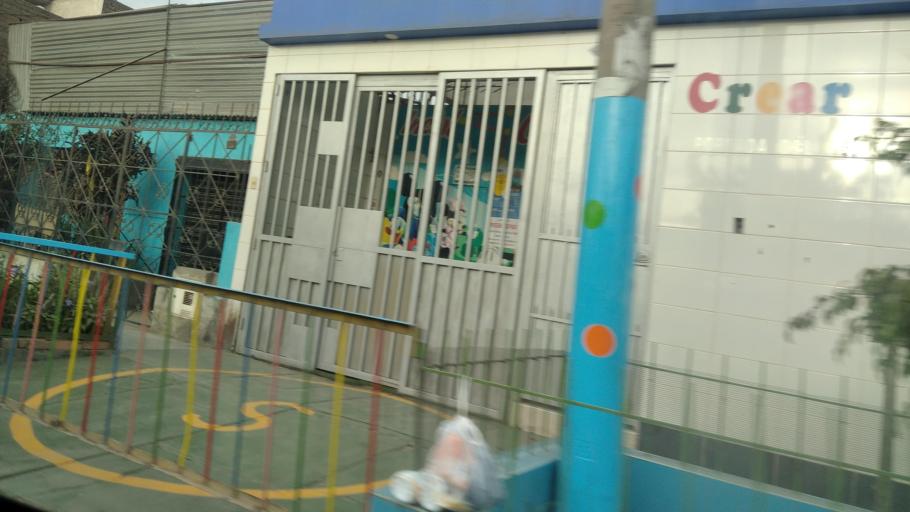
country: PE
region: Lima
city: Lima
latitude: -12.0257
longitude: -76.9962
